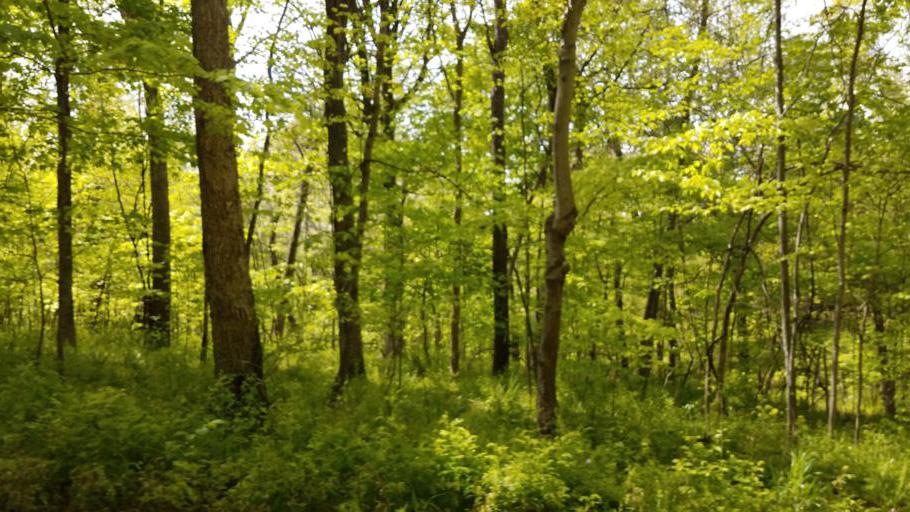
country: US
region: Ohio
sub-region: Knox County
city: Gambier
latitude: 40.3890
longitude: -82.3295
